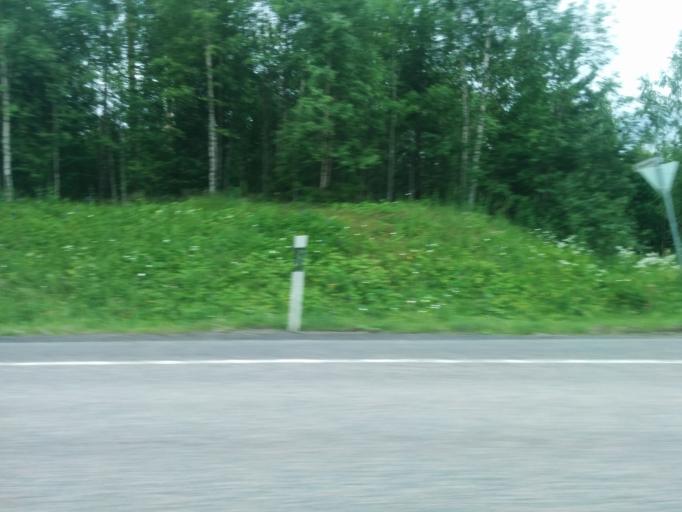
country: FI
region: Pirkanmaa
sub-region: Tampere
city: Orivesi
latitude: 61.7041
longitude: 24.4432
